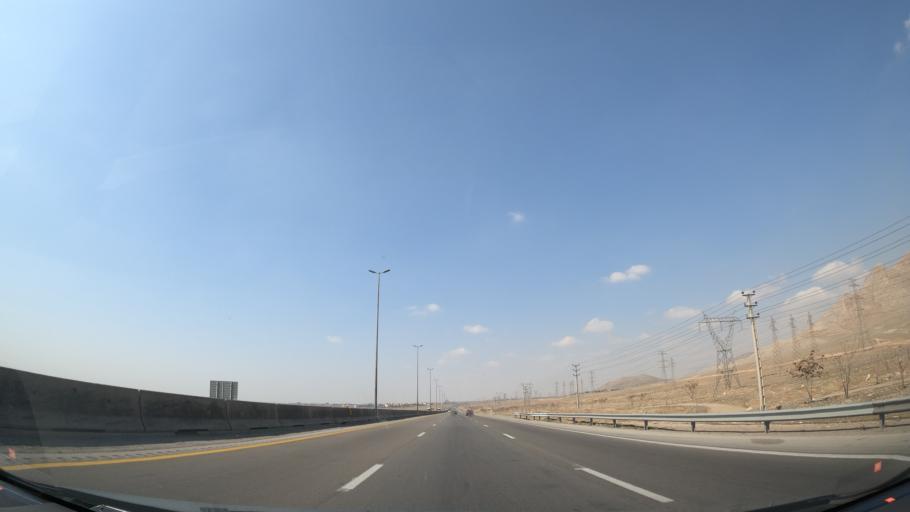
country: IR
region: Qazvin
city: Abyek
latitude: 36.0551
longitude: 50.5089
